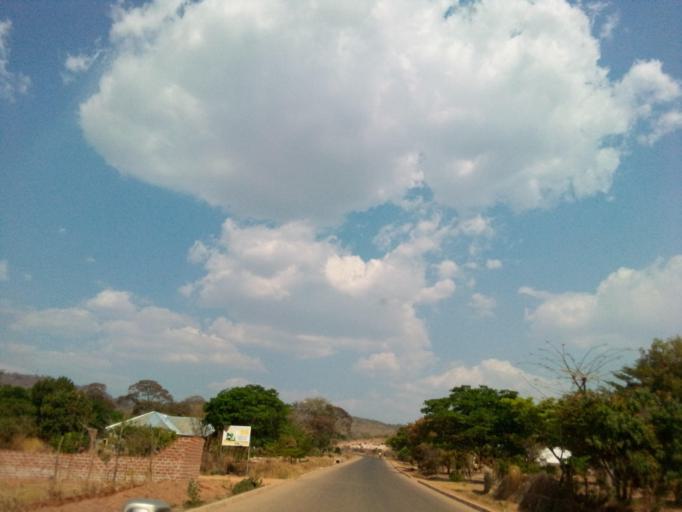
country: ZM
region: Northern
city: Mpika
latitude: -11.8464
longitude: 31.4499
